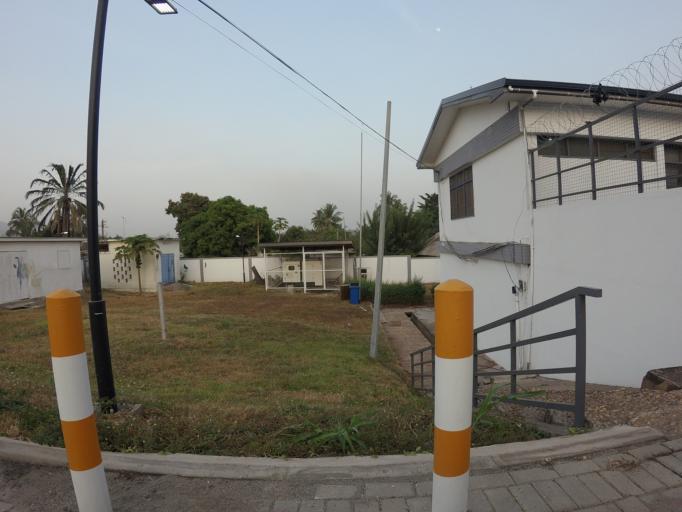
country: GH
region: Volta
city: Ho
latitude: 6.6108
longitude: 0.4710
